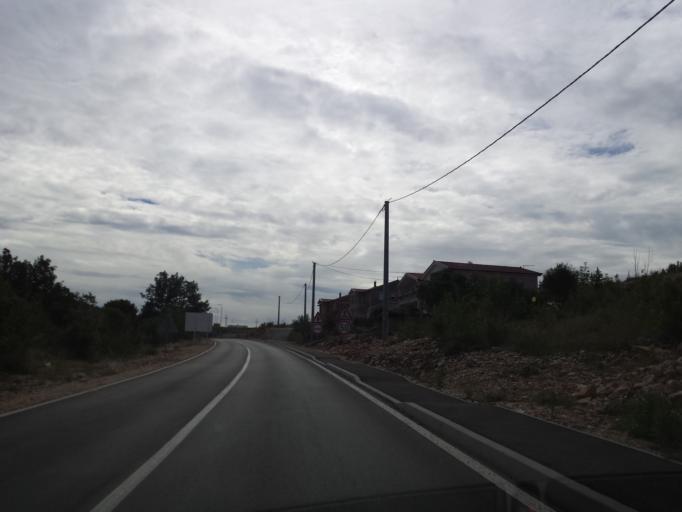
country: BA
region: Federation of Bosnia and Herzegovina
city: Capljina
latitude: 43.1652
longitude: 17.6552
